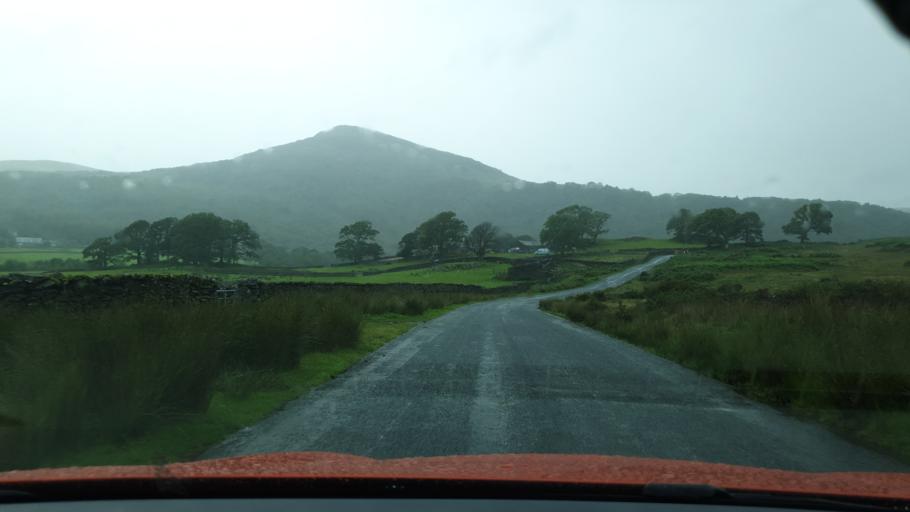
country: GB
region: England
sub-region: Cumbria
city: Millom
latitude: 54.3197
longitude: -3.2343
